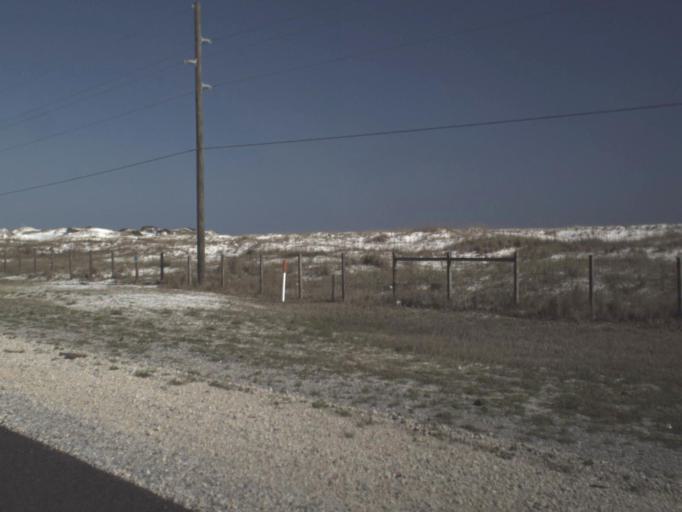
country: US
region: Florida
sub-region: Okaloosa County
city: Lake Lorraine
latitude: 30.3948
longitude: -86.5687
